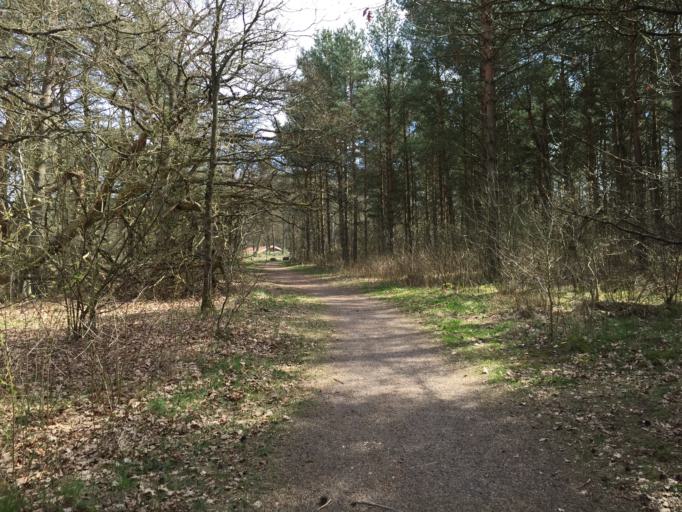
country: SE
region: Skane
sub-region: Lunds Kommun
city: Veberod
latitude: 55.6224
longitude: 13.4990
